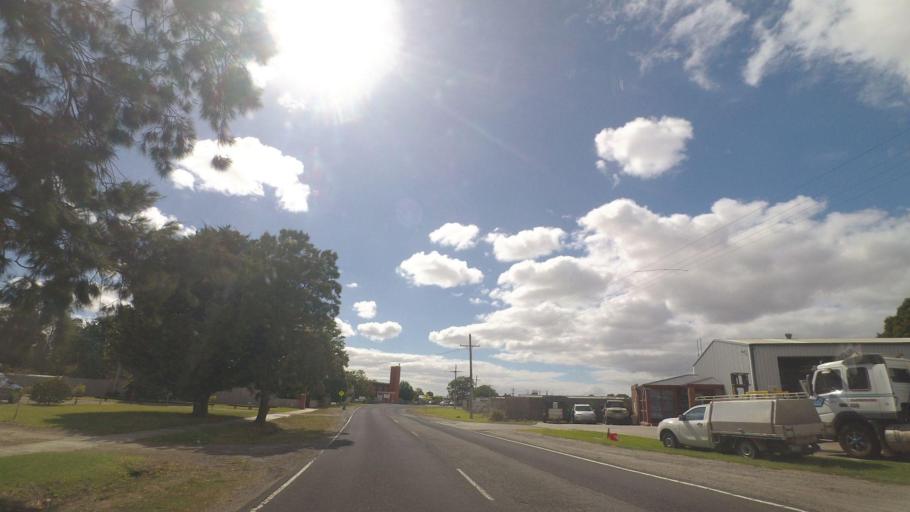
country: AU
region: Victoria
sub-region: Cardinia
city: Koo-Wee-Rup
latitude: -38.1979
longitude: 145.4838
